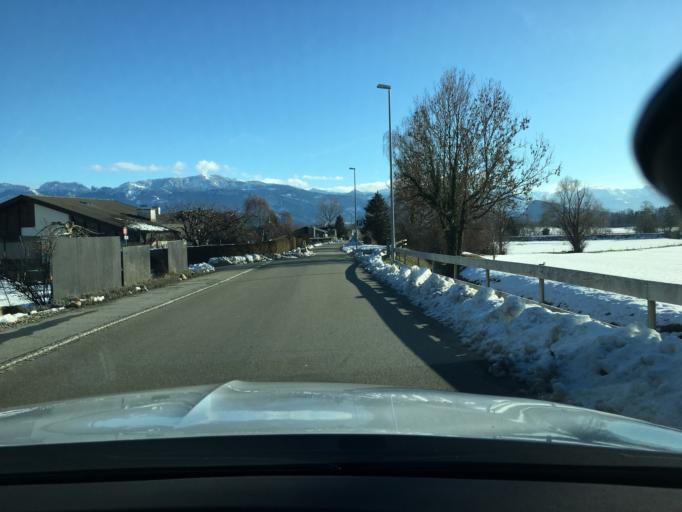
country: CH
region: Saint Gallen
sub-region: Wahlkreis Rheintal
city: Rebstein
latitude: 47.3902
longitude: 9.5725
